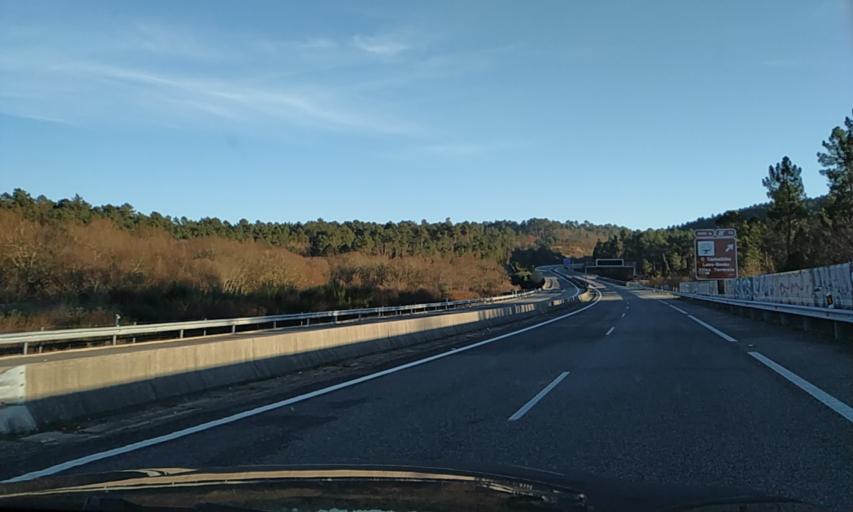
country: ES
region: Galicia
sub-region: Provincia de Ourense
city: Cea
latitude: 42.4645
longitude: -8.0269
